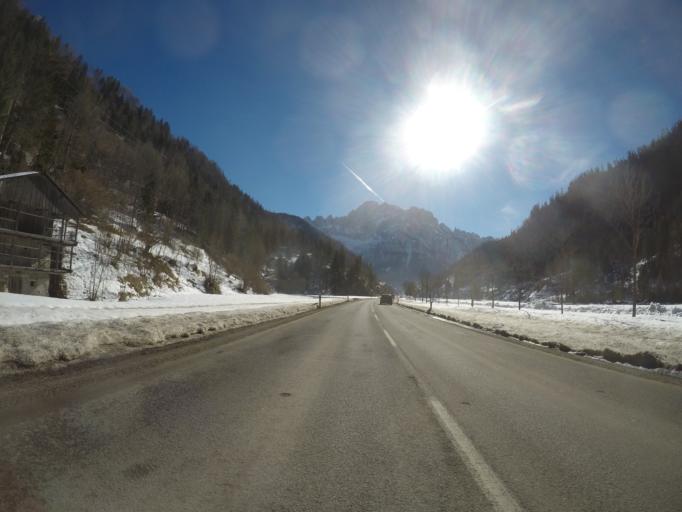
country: IT
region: Veneto
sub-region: Provincia di Belluno
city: Colle Santa Lucia
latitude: 46.4319
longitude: 11.9999
